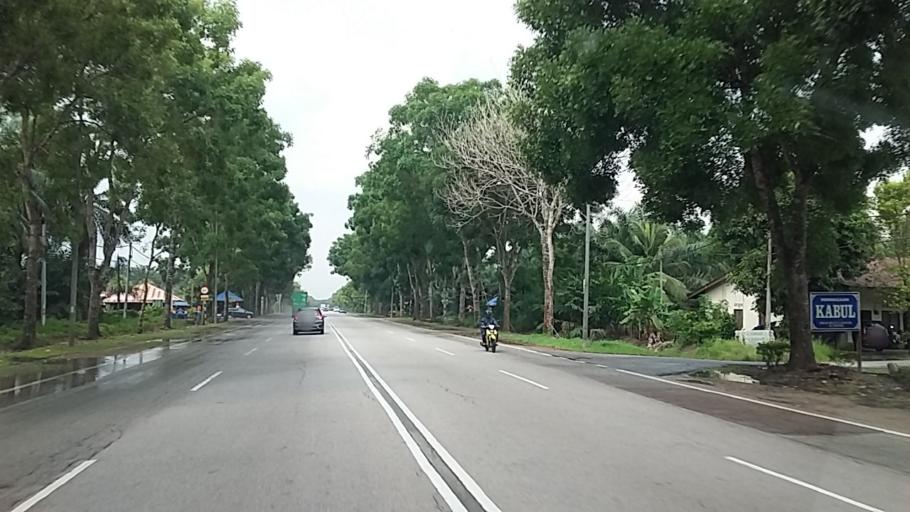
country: MY
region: Johor
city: Parit Raja
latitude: 1.8720
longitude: 103.1321
